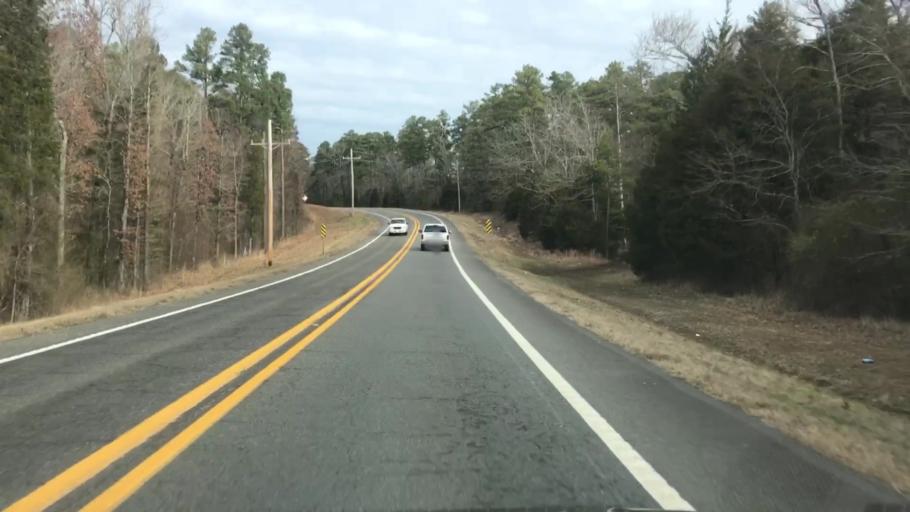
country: US
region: Arkansas
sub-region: Montgomery County
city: Mount Ida
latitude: 34.5865
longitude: -93.6634
